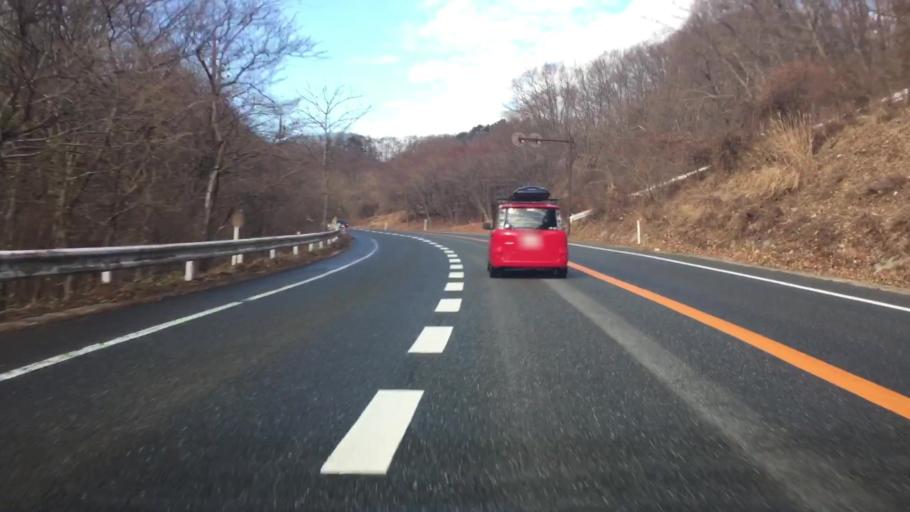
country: JP
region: Nagano
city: Saku
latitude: 36.3026
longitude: 138.6711
